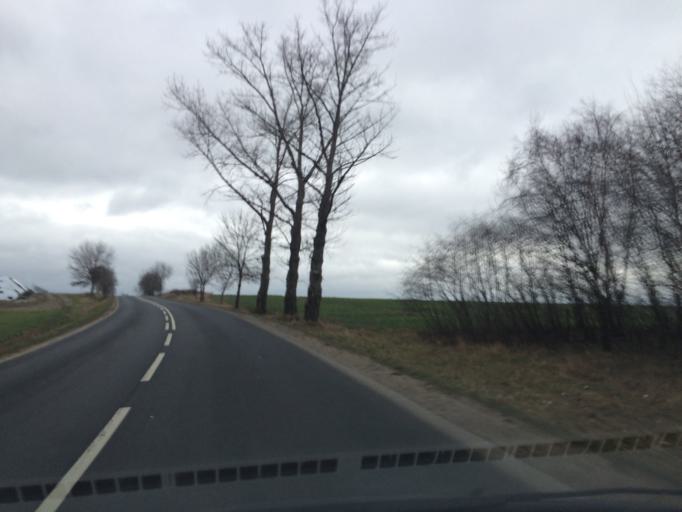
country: PL
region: Lower Silesian Voivodeship
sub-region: Powiat lubanski
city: Pisarzowice
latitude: 51.1562
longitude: 15.2668
